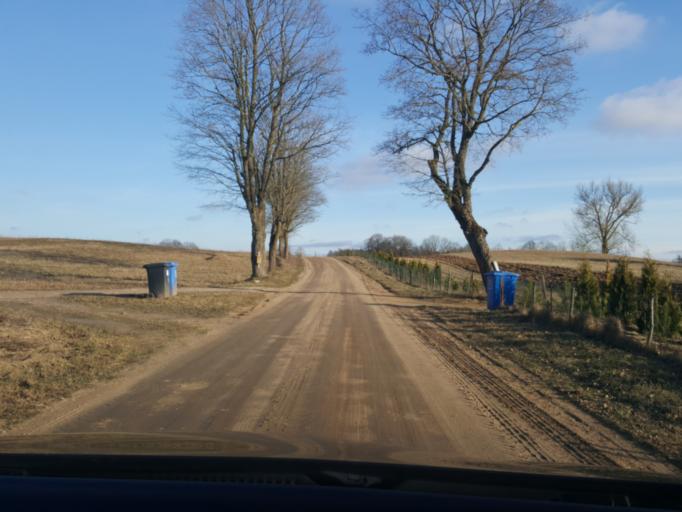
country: LT
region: Alytaus apskritis
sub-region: Alytus
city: Alytus
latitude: 54.3437
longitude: 23.8666
